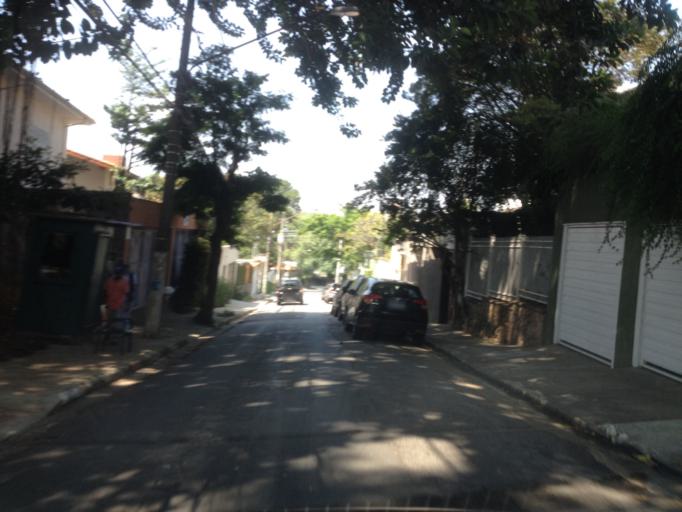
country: BR
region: Sao Paulo
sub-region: Sao Paulo
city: Sao Paulo
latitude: -23.5445
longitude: -46.6796
